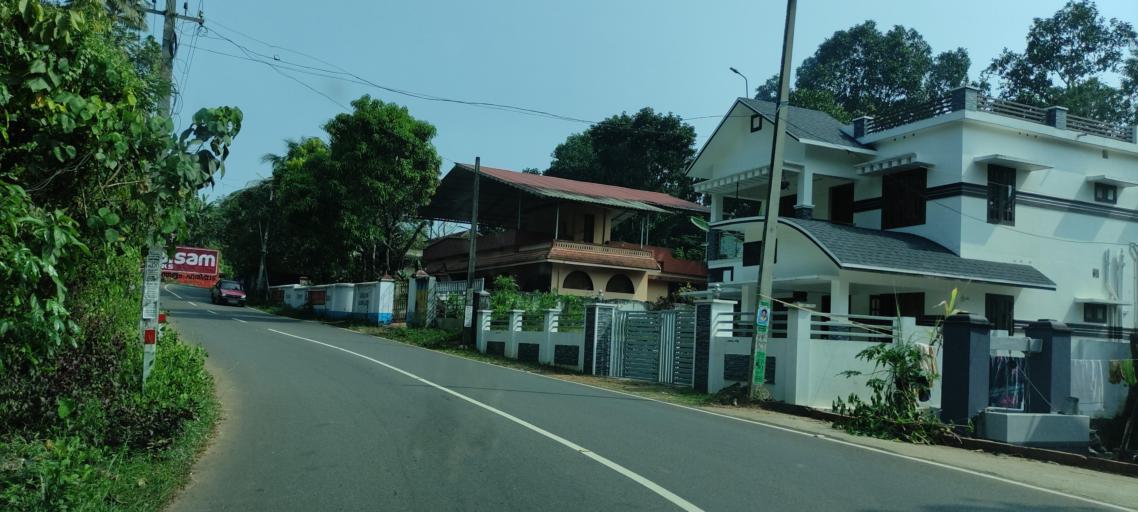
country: IN
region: Kerala
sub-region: Pattanamtitta
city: Adur
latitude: 9.2418
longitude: 76.6815
